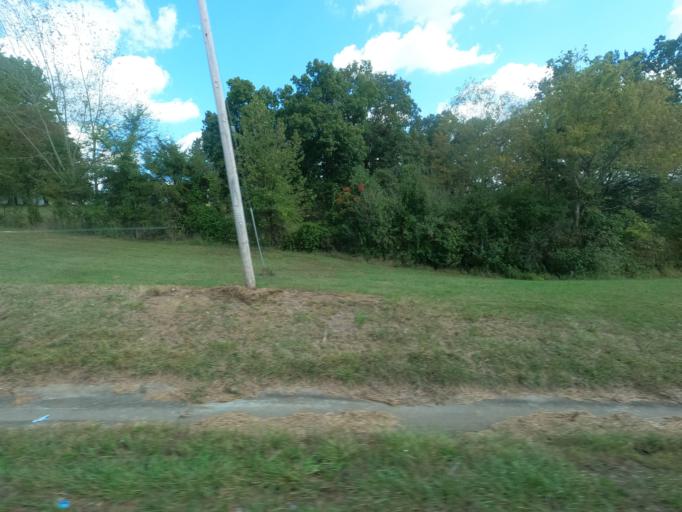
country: US
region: Illinois
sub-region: Johnson County
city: Vienna
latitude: 37.4303
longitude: -88.8928
